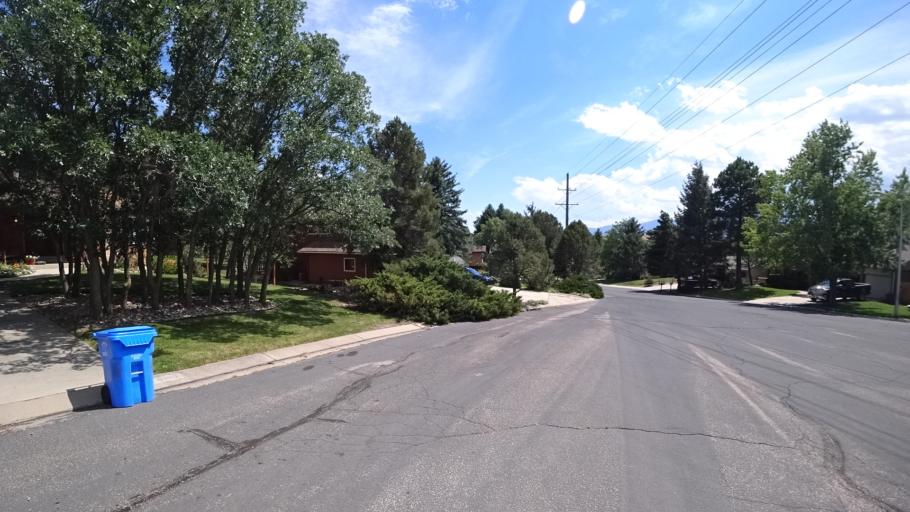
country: US
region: Colorado
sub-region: El Paso County
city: Air Force Academy
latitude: 38.9329
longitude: -104.8289
